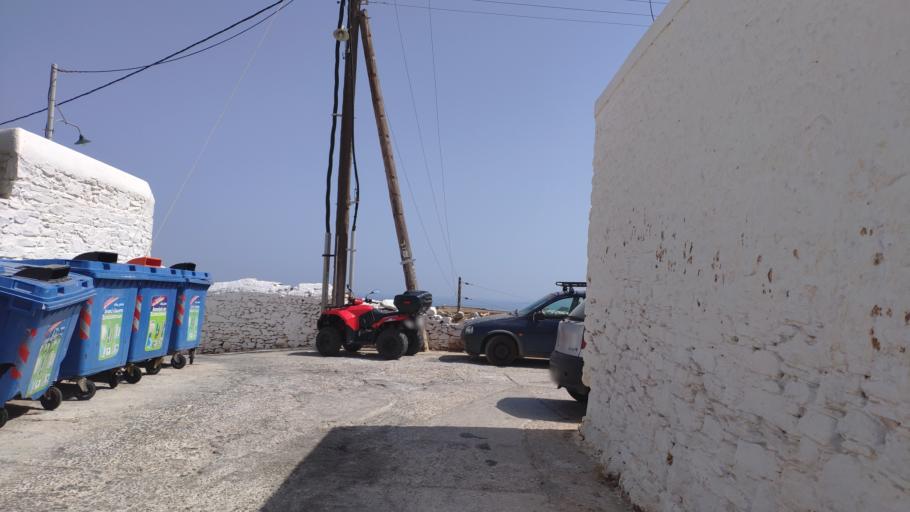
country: GR
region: South Aegean
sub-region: Nomos Kykladon
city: Kythnos
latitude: 37.4130
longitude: 24.4300
